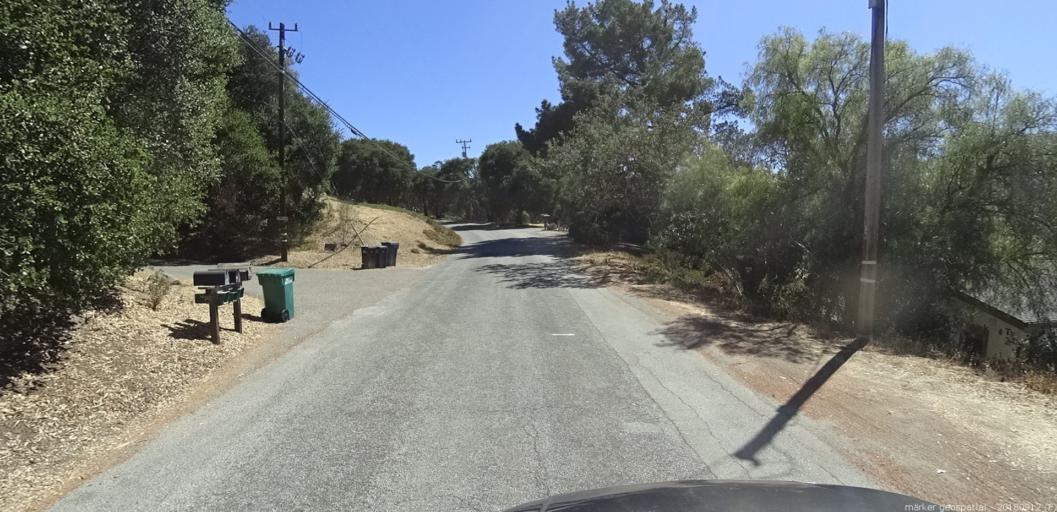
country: US
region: California
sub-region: Monterey County
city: Carmel Valley Village
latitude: 36.4952
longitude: -121.7429
